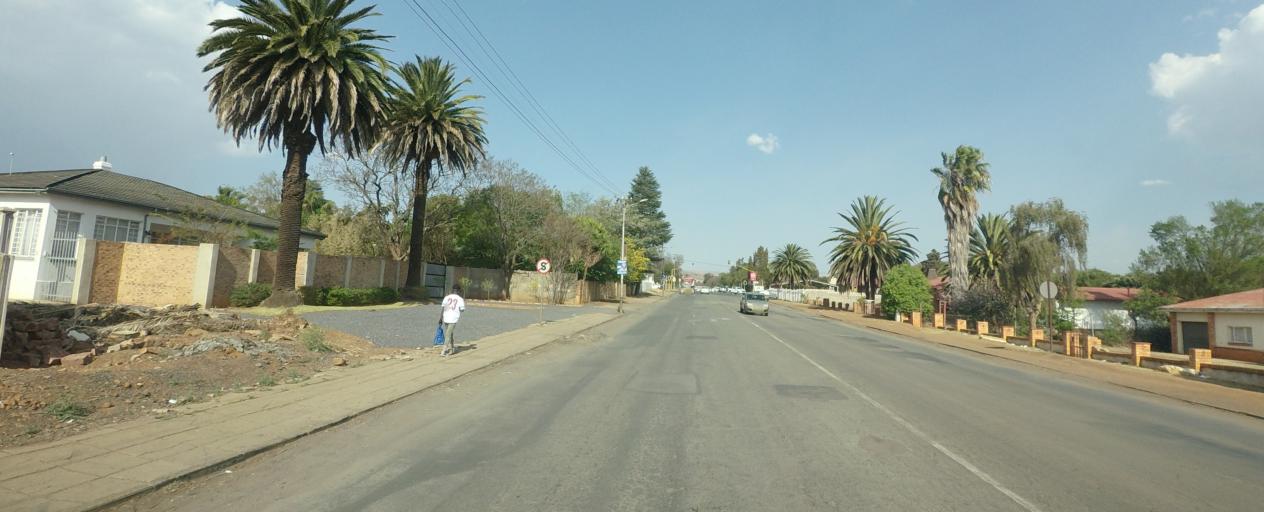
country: ZA
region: Mpumalanga
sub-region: Ehlanzeni District
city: Lydenburg
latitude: -25.0970
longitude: 30.4590
